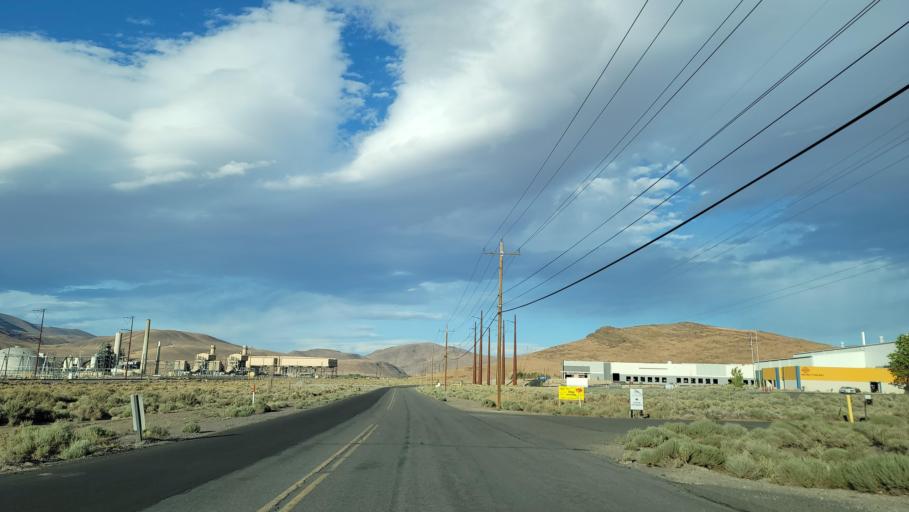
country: US
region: Nevada
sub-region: Washoe County
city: Spanish Springs
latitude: 39.5569
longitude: -119.5347
